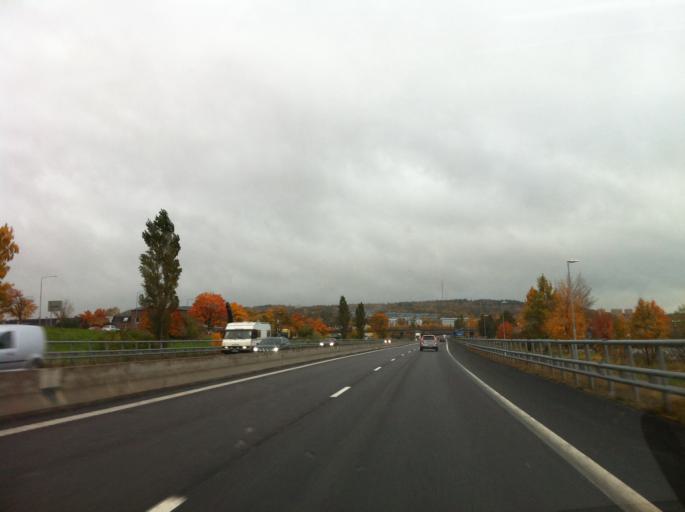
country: SE
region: Joenkoeping
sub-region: Jonkopings Kommun
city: Huskvarna
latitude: 57.8015
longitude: 14.2714
